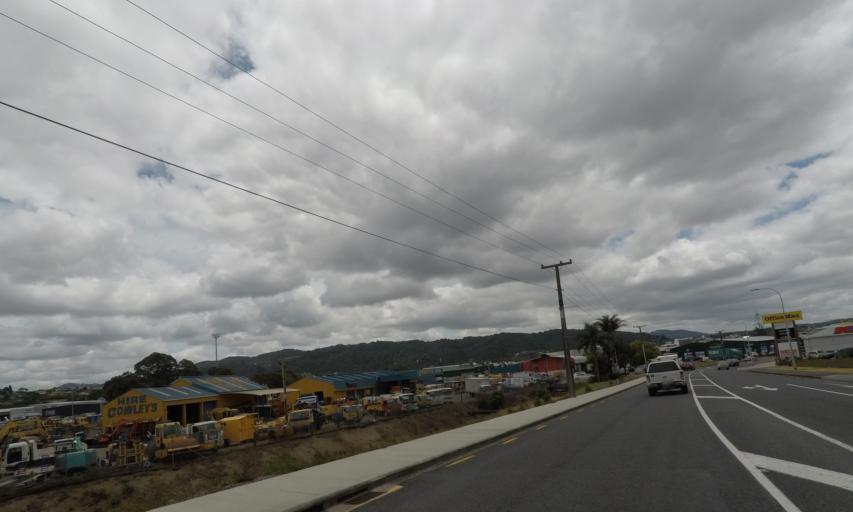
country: NZ
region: Northland
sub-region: Whangarei
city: Whangarei
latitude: -35.7327
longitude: 174.3270
